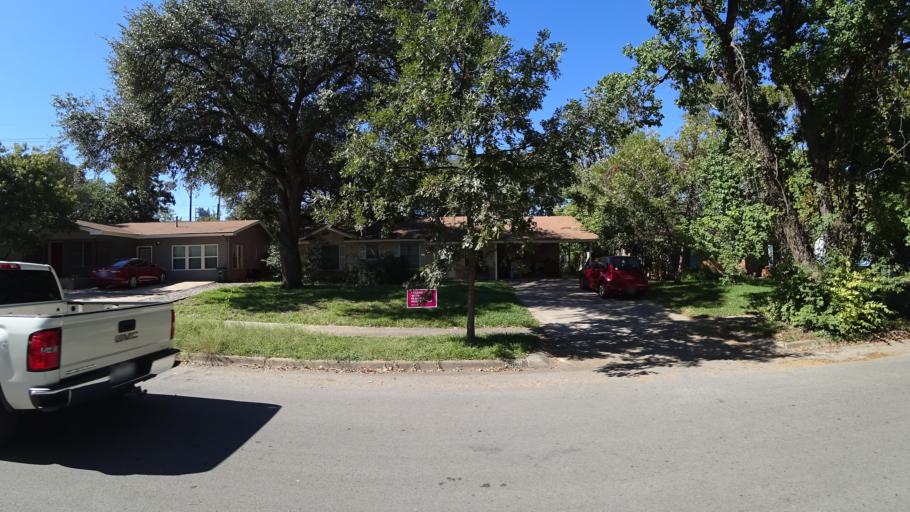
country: US
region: Texas
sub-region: Travis County
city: West Lake Hills
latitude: 30.3379
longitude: -97.7533
